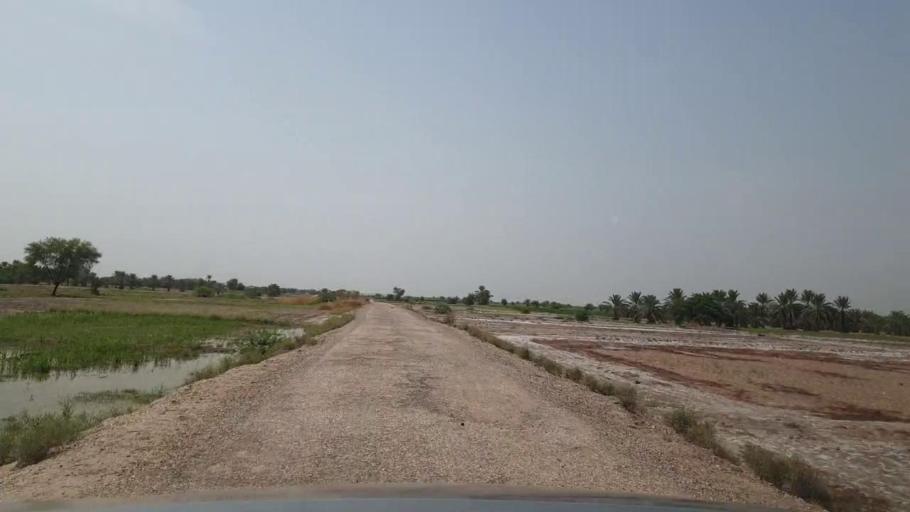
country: PK
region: Sindh
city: Pano Aqil
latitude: 27.6160
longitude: 69.1418
